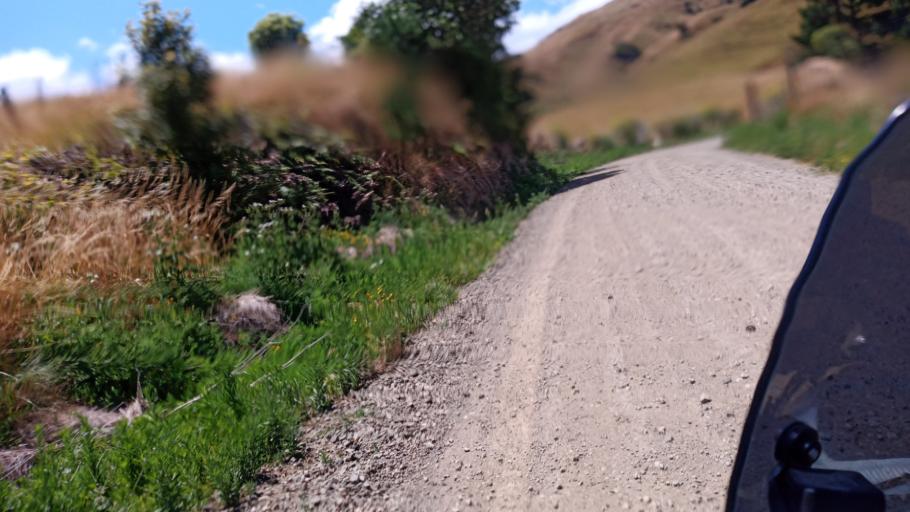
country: NZ
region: Bay of Plenty
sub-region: Opotiki District
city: Opotiki
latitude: -38.4462
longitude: 177.5383
